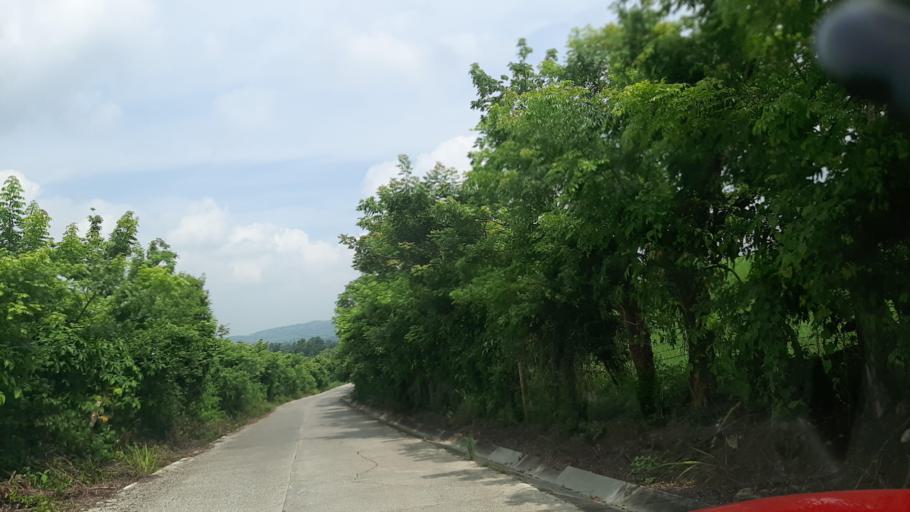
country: MX
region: Veracruz
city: Gutierrez Zamora
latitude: 20.4461
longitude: -97.1742
